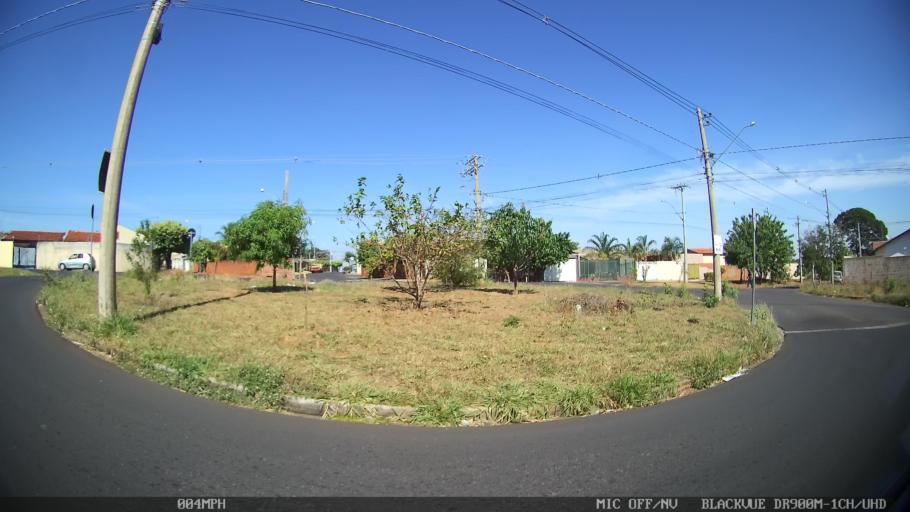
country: BR
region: Sao Paulo
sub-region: Sao Jose Do Rio Preto
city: Sao Jose do Rio Preto
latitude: -20.7663
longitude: -49.4128
